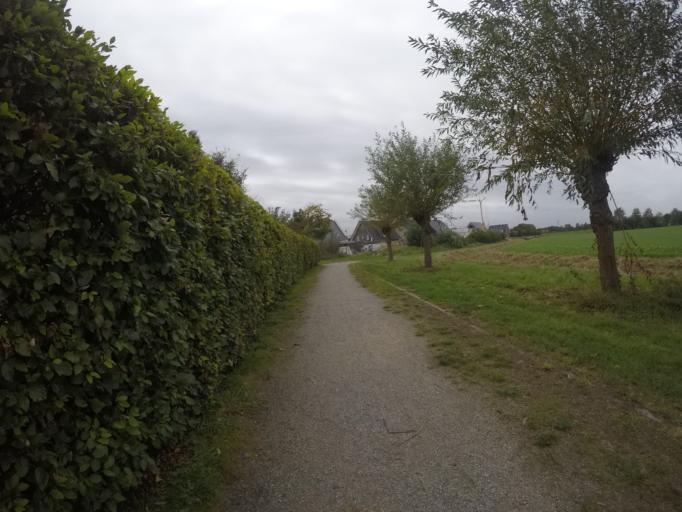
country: DE
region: North Rhine-Westphalia
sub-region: Regierungsbezirk Munster
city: Rhede
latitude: 51.8491
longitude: 6.6879
